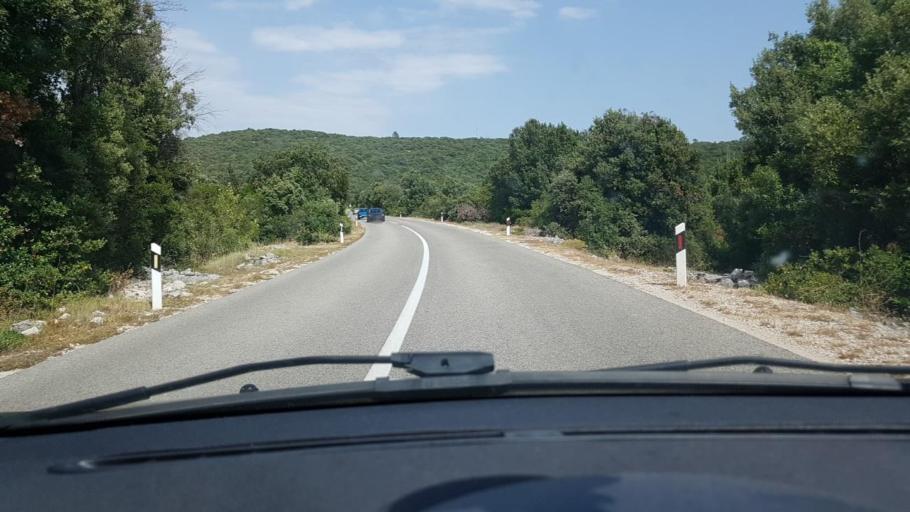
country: HR
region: Dubrovacko-Neretvanska
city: Smokvica
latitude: 42.9478
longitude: 16.9966
